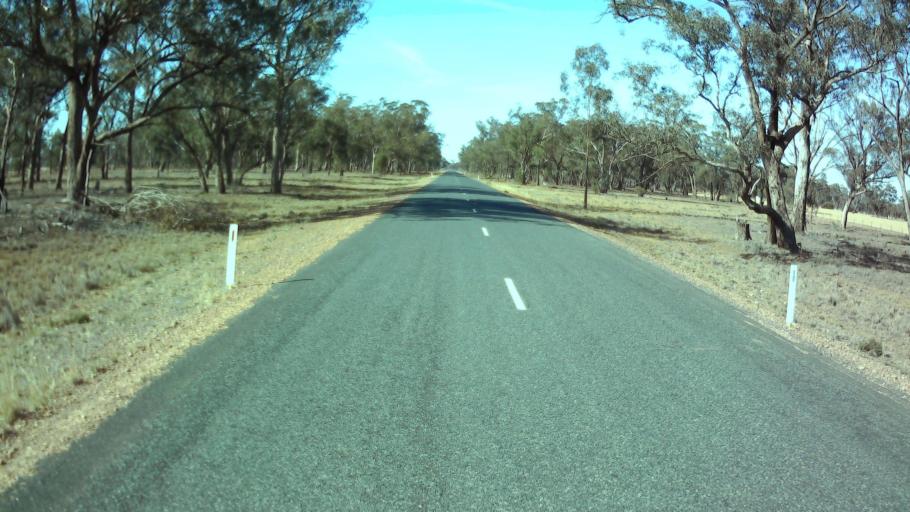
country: AU
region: New South Wales
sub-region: Weddin
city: Grenfell
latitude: -34.0613
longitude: 147.9096
